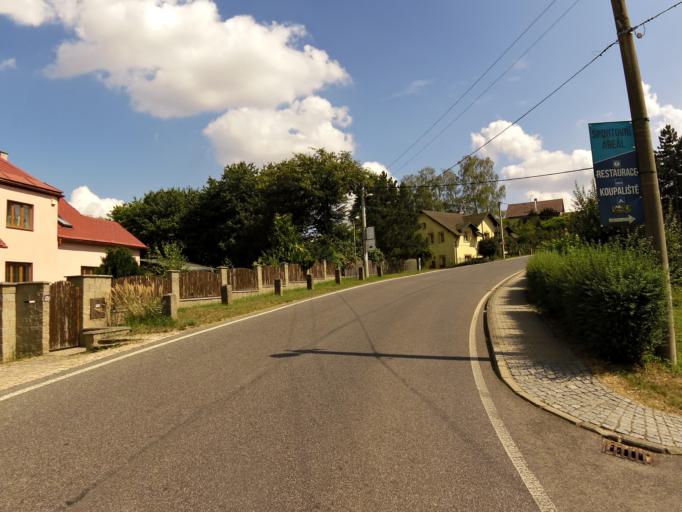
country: CZ
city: Prisovice
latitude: 50.5864
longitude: 15.0478
